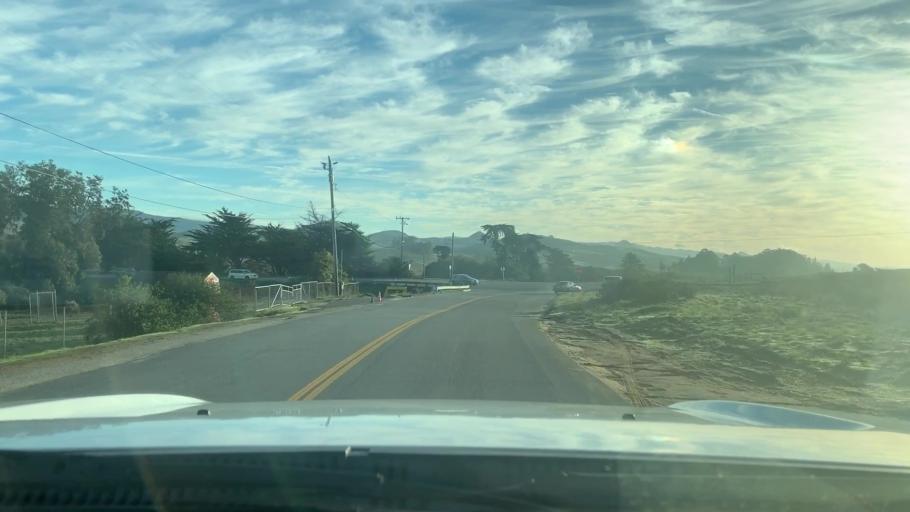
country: US
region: California
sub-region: San Luis Obispo County
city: Los Osos
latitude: 35.3225
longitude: -120.8230
